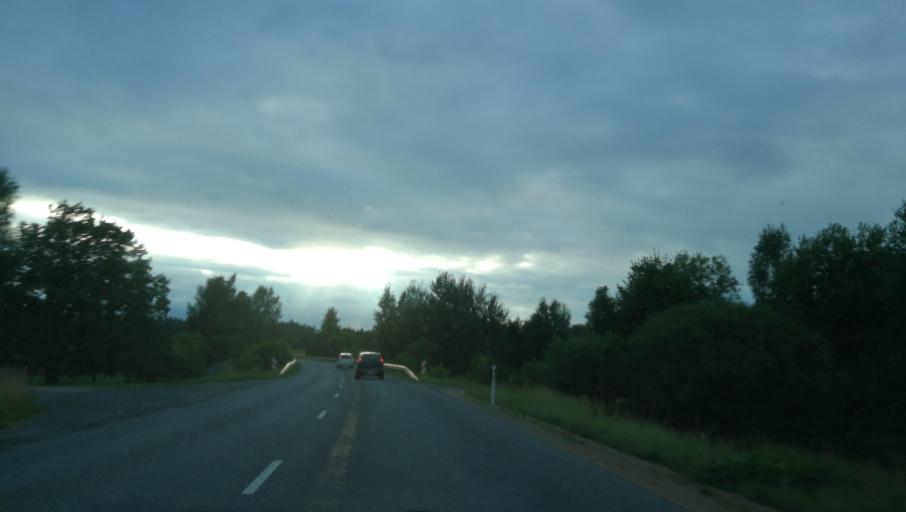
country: LV
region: Sigulda
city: Sigulda
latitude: 57.0267
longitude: 24.8070
